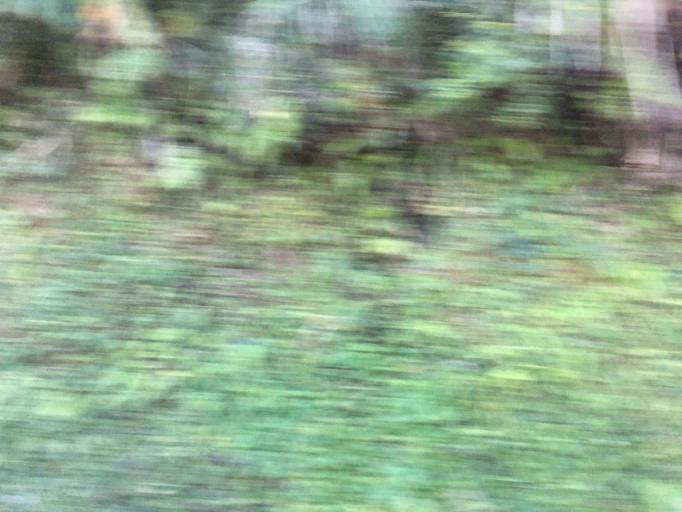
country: TW
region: Taiwan
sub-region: Yilan
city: Yilan
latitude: 24.5396
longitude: 121.5151
